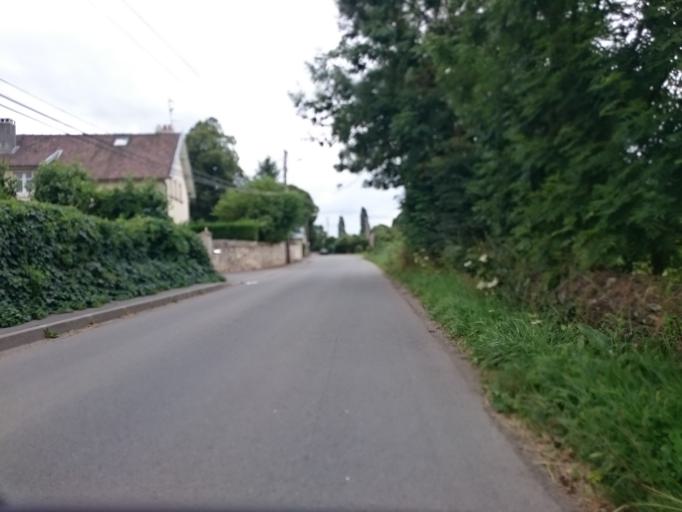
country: FR
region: Lower Normandy
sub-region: Departement du Calvados
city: Fleury-sur-Orne
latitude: 49.1432
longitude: -0.3879
